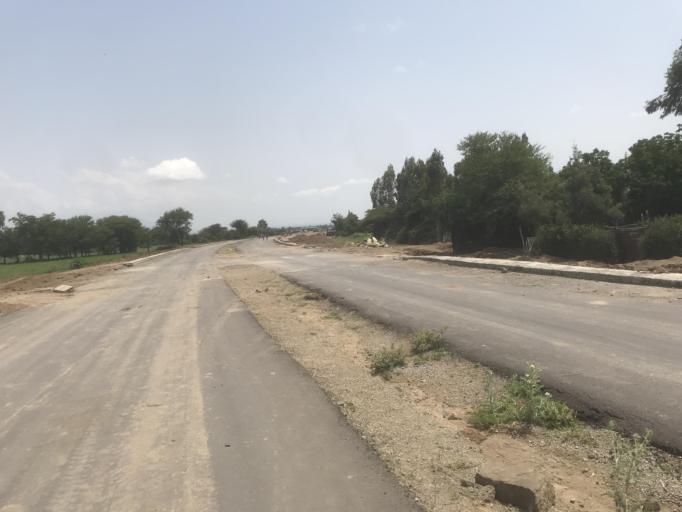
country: ET
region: Oromiya
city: Mojo
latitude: 8.2951
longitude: 38.9400
